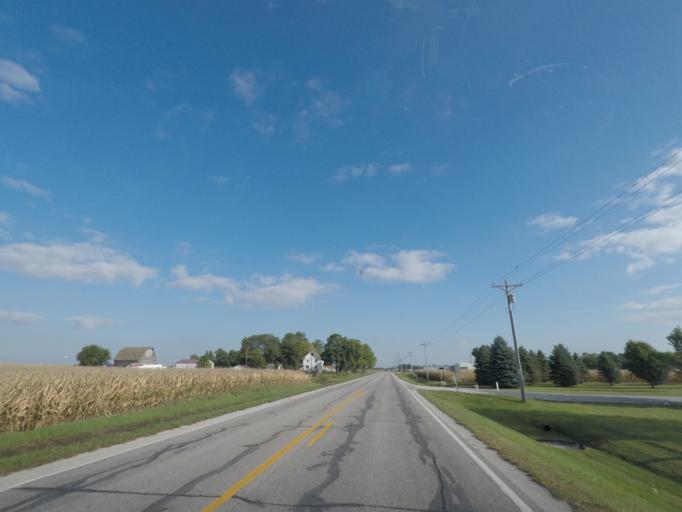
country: US
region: Iowa
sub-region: Story County
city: Nevada
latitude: 41.9992
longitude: -93.4628
